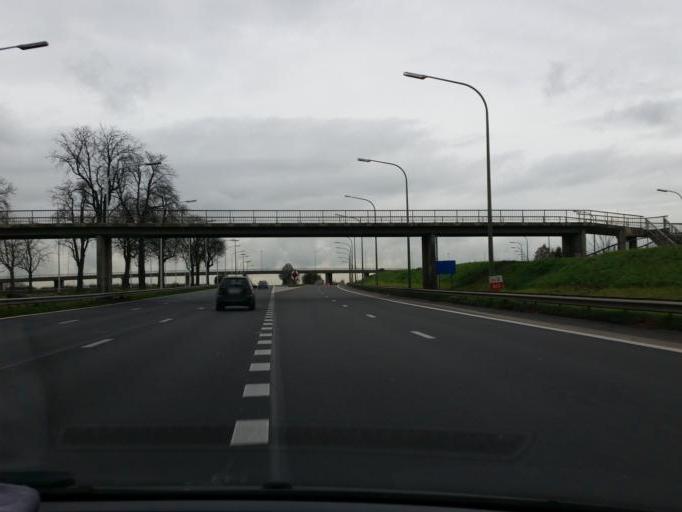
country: BE
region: Flanders
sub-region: Provincie Vlaams-Brabant
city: Bever
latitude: 50.9081
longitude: 4.3447
